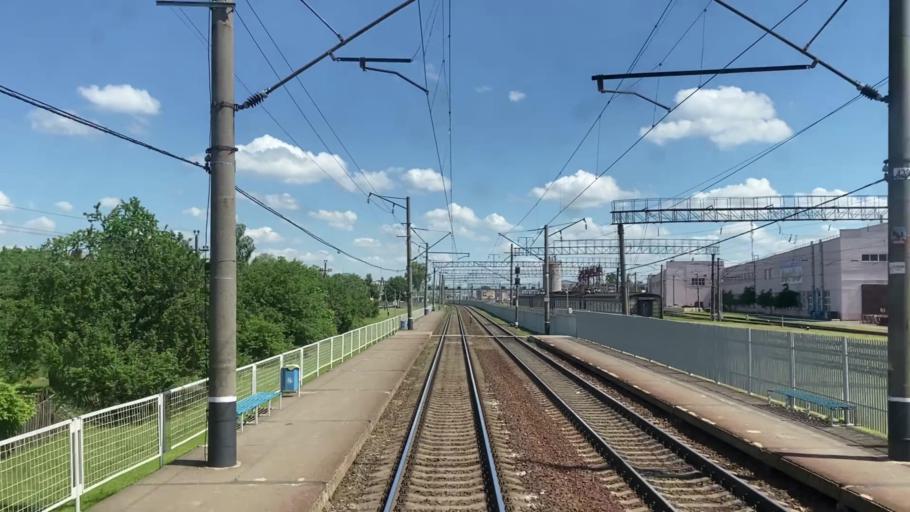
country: BY
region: Brest
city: Baranovichi
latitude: 53.1194
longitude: 25.9710
